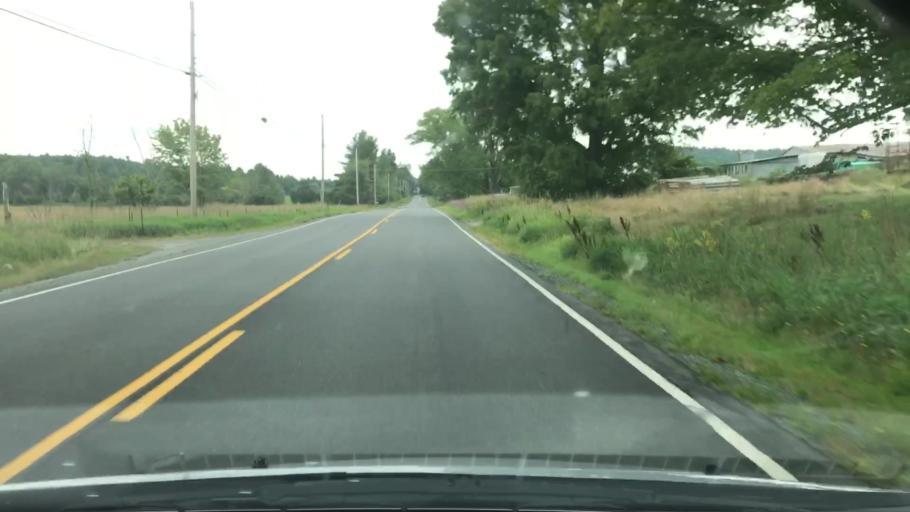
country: US
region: New Hampshire
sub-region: Grafton County
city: Haverhill
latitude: 43.9966
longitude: -72.0758
